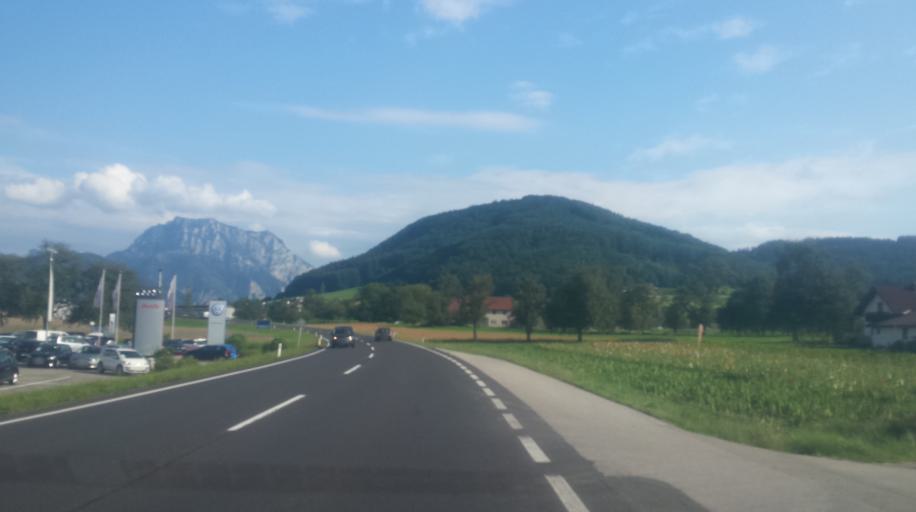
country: AT
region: Upper Austria
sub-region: Politischer Bezirk Gmunden
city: Altmunster
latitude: 47.9378
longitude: 13.7580
